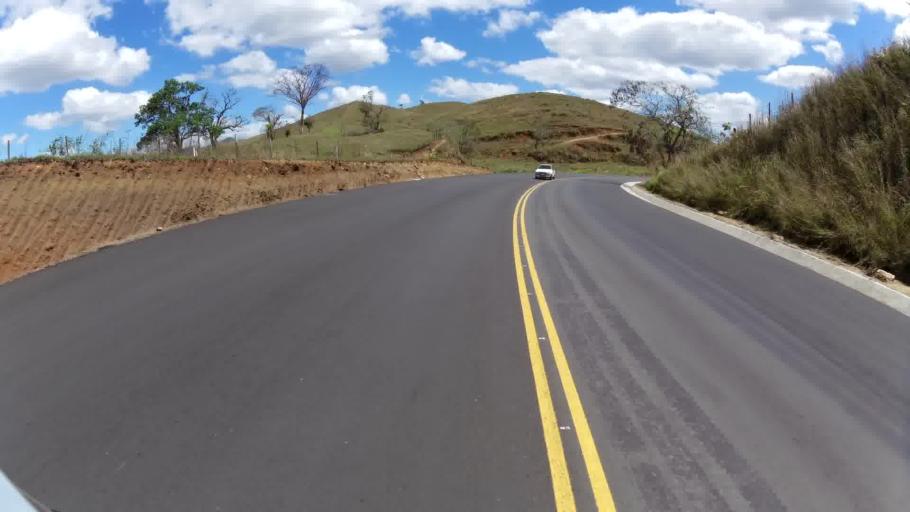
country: BR
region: Rio de Janeiro
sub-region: Itaperuna
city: Itaperuna
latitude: -21.2917
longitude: -41.8053
